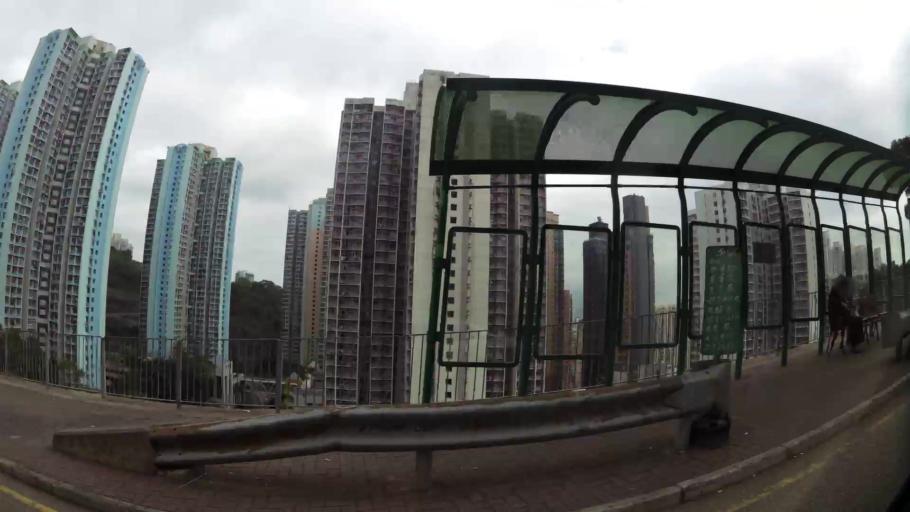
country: HK
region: Wanchai
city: Wan Chai
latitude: 22.2792
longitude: 114.2208
